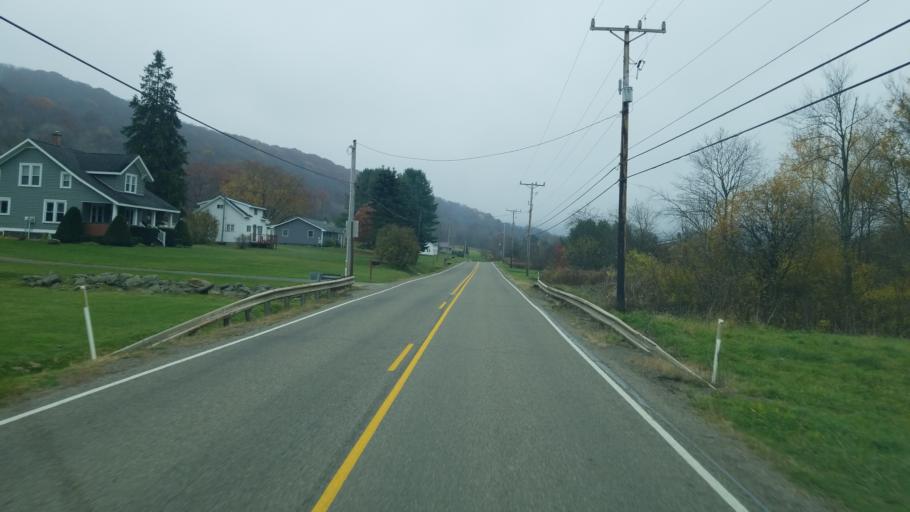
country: US
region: Pennsylvania
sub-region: McKean County
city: Smethport
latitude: 41.8724
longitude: -78.4801
